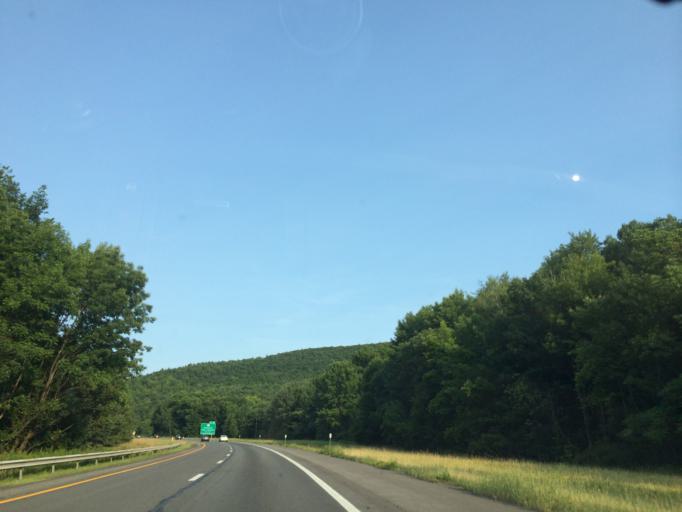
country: US
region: Massachusetts
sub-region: Berkshire County
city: Richmond
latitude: 42.3681
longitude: -73.4566
